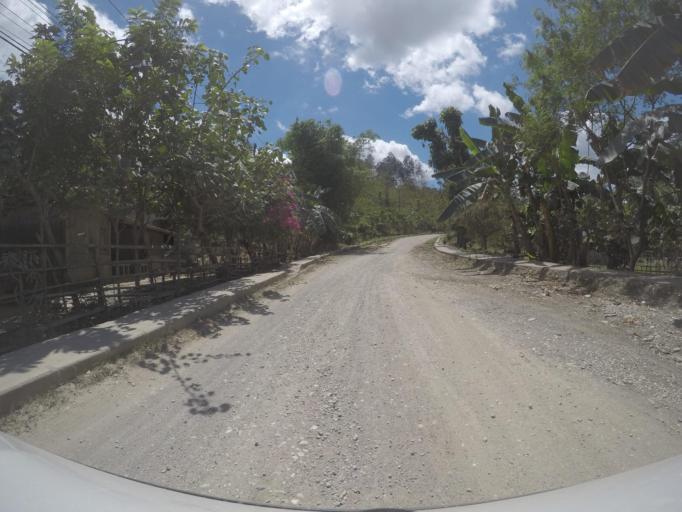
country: TL
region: Viqueque
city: Viqueque
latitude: -8.8471
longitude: 126.3669
